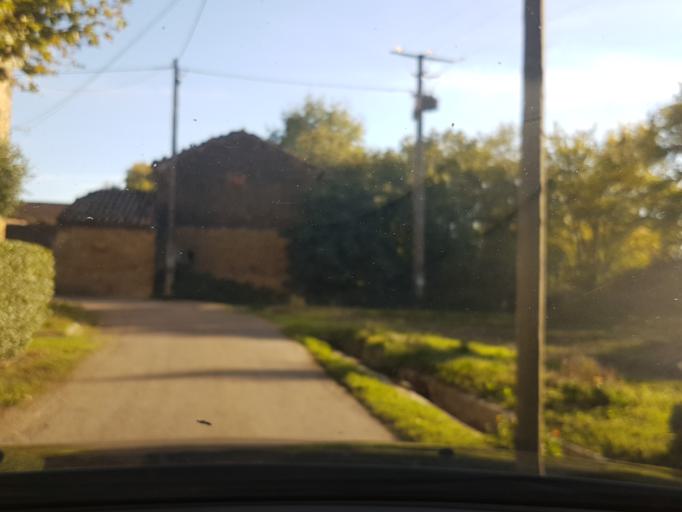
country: FR
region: Provence-Alpes-Cote d'Azur
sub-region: Departement du Vaucluse
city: Althen-des-Paluds
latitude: 44.0306
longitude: 4.9396
